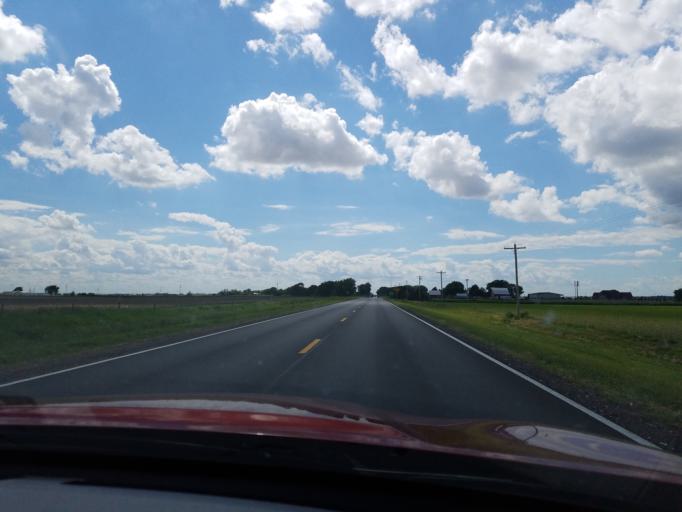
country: US
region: Nebraska
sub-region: Buffalo County
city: Kearney
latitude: 40.6411
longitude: -99.0771
